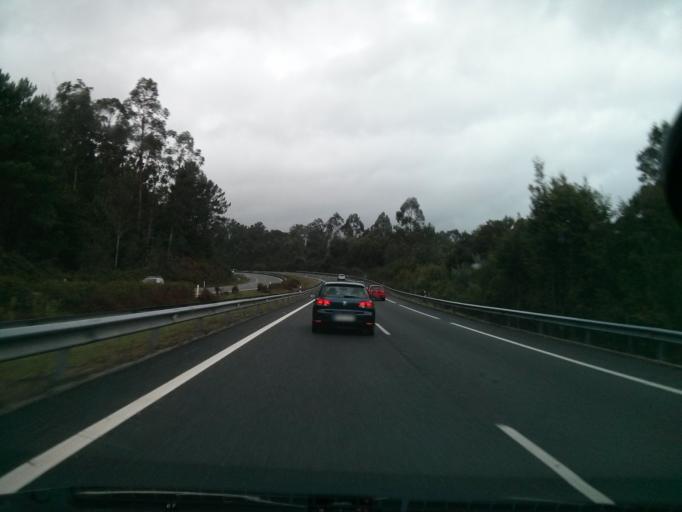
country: ES
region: Galicia
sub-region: Provincia de Pontevedra
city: Ponteareas
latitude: 42.1690
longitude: -8.5413
